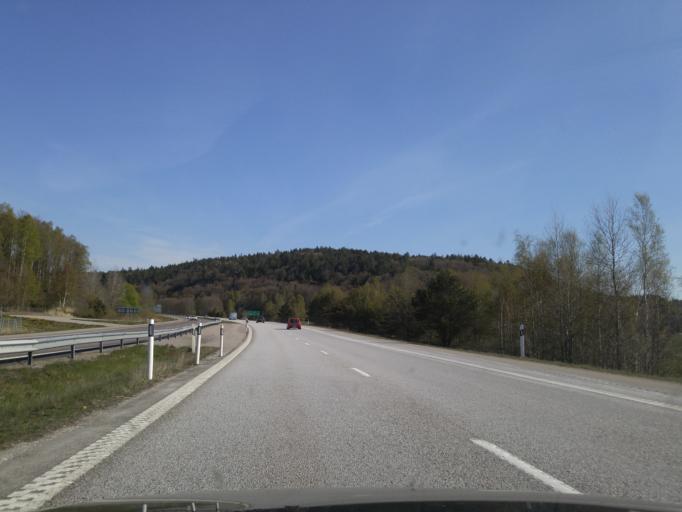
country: SE
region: Vaestra Goetaland
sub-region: Stenungsunds Kommun
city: Stenungsund
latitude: 58.0661
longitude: 11.8894
